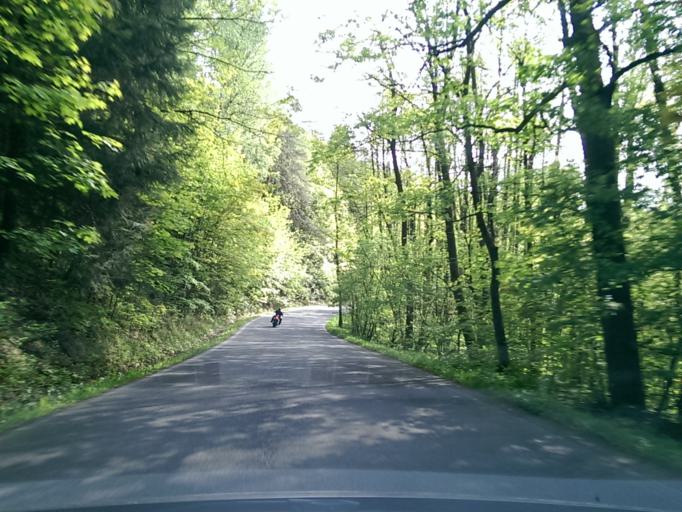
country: CZ
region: Central Bohemia
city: Bela pod Bezdezem
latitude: 50.4961
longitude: 14.8574
